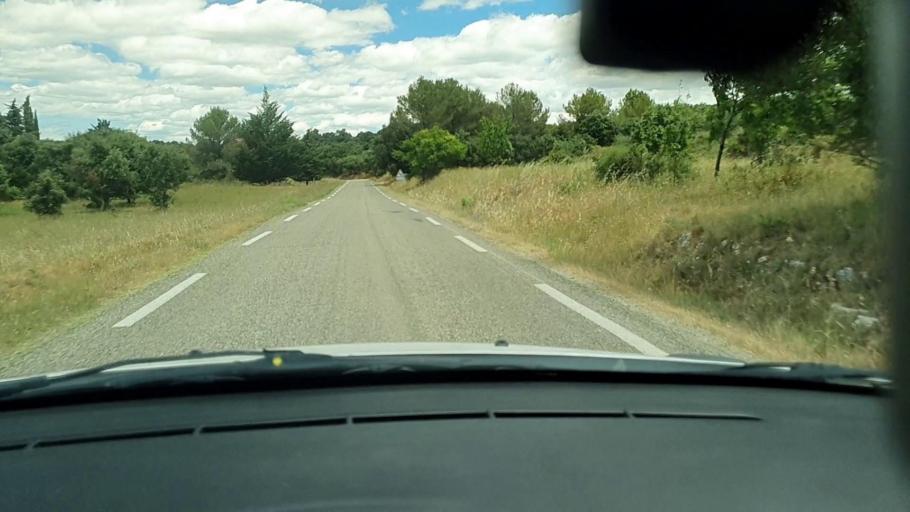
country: FR
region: Languedoc-Roussillon
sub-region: Departement du Gard
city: Cabrieres
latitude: 43.9219
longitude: 4.4737
